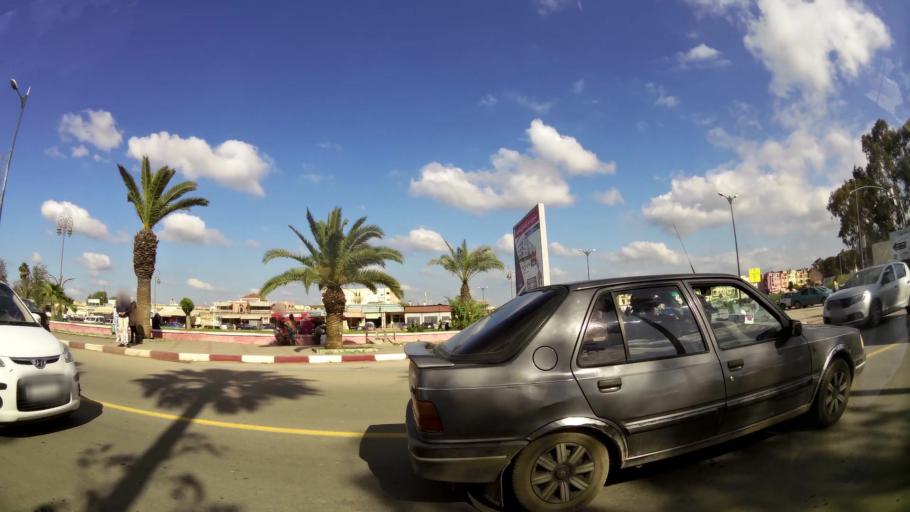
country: MA
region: Chaouia-Ouardigha
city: Nouaseur
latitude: 33.3730
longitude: -7.5420
